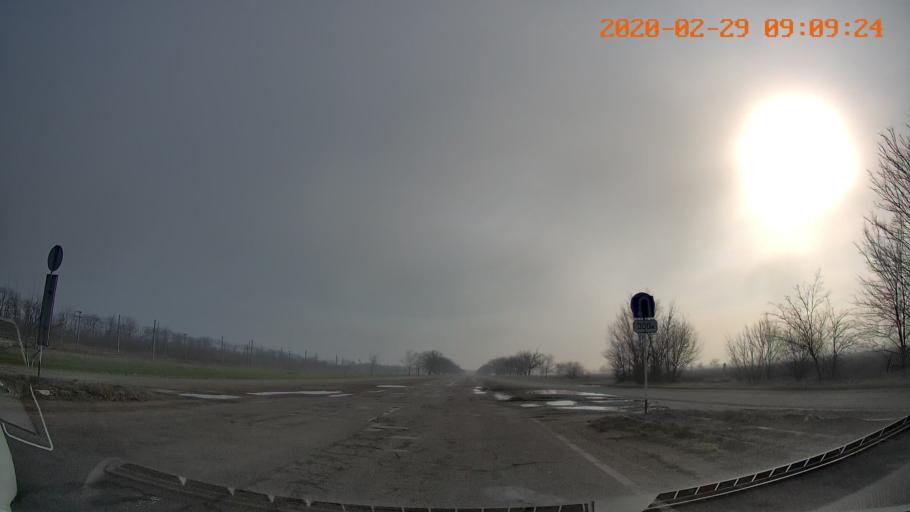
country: MD
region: Telenesti
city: Slobozia
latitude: 46.8449
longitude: 29.7619
